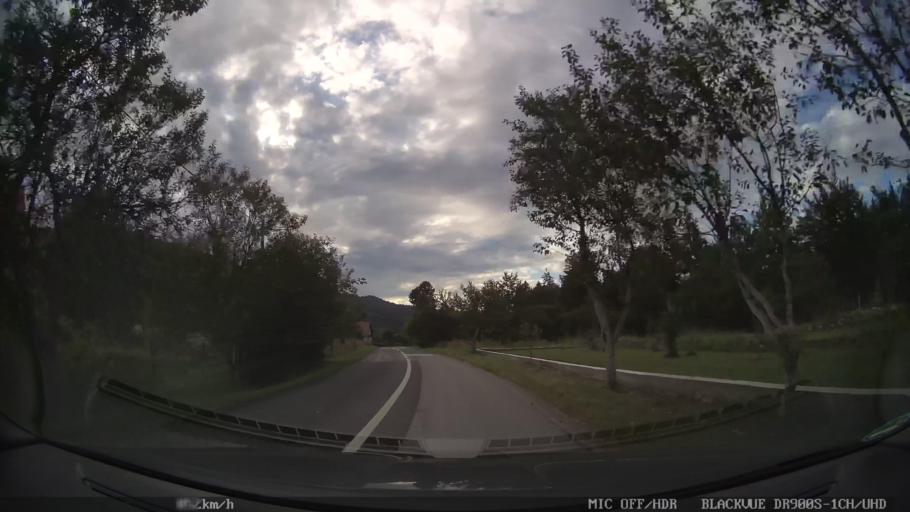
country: HR
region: Licko-Senjska
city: Jezerce
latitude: 44.9476
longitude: 15.5381
